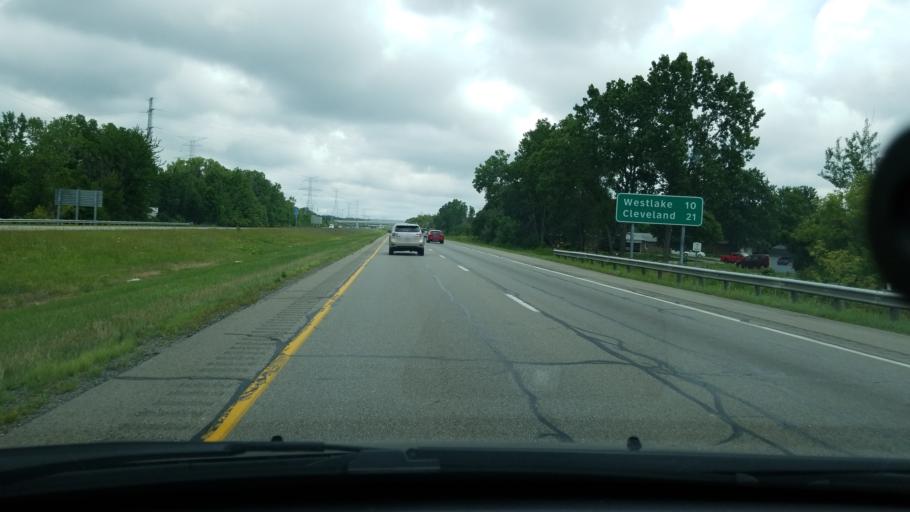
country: US
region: Ohio
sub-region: Lorain County
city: Sheffield
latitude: 41.4369
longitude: -82.0800
